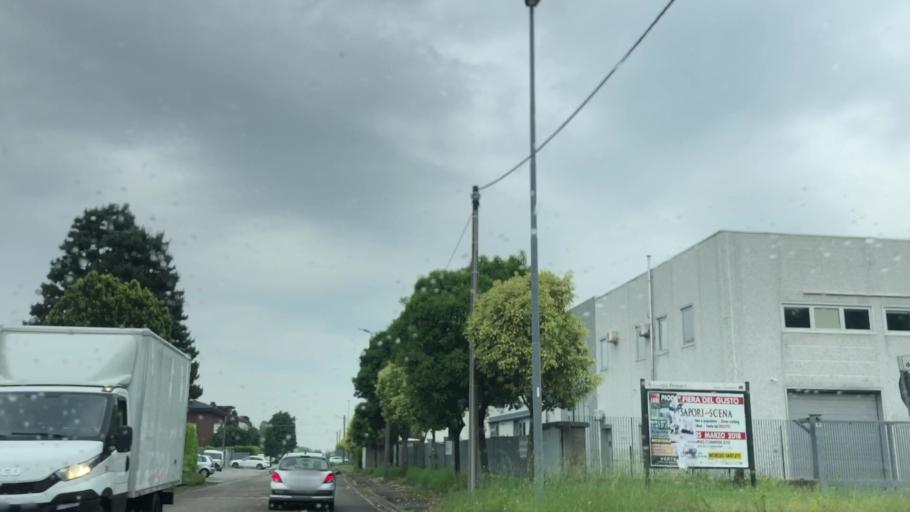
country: IT
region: Lombardy
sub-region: Provincia di Como
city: Fenegro
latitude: 45.6947
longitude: 8.9948
